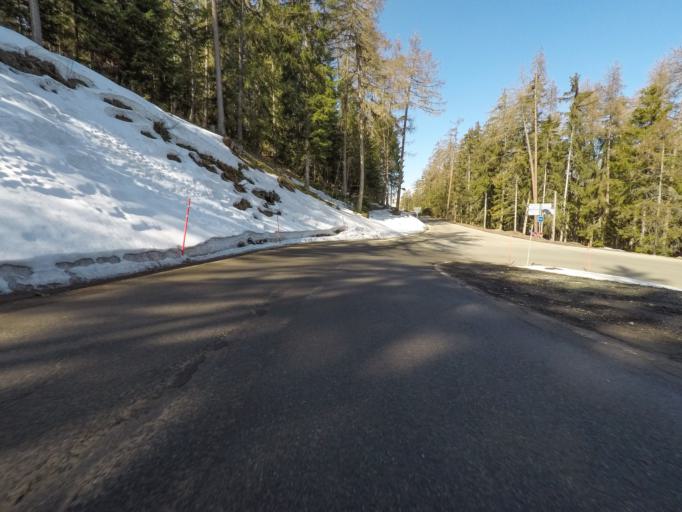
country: CH
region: Valais
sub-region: Herens District
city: Vex
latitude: 46.1987
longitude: 7.3812
